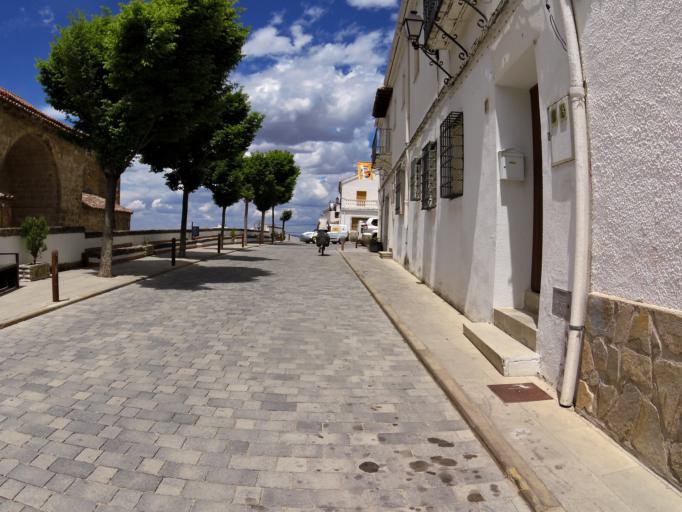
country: ES
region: Andalusia
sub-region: Provincia de Jaen
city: Segura de la Sierra
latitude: 38.2981
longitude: -2.6518
